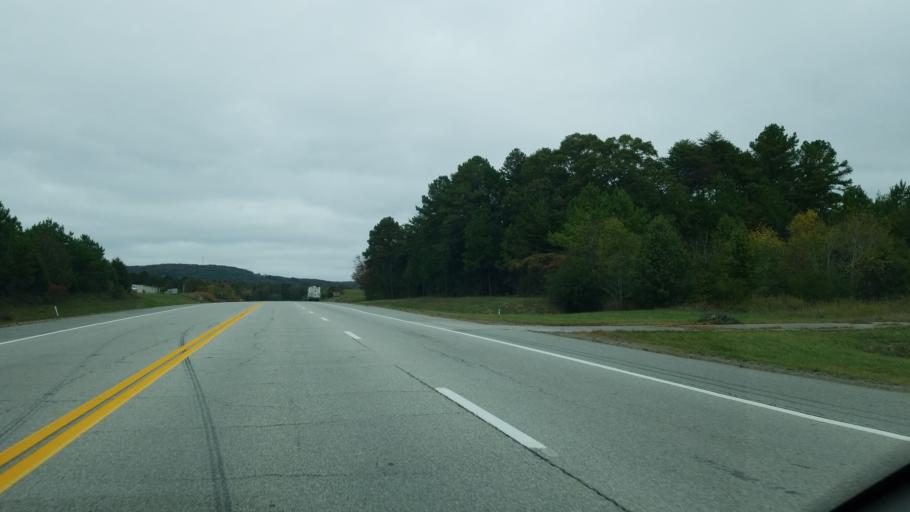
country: US
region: Tennessee
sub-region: Rhea County
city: Dayton
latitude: 35.4639
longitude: -85.0171
